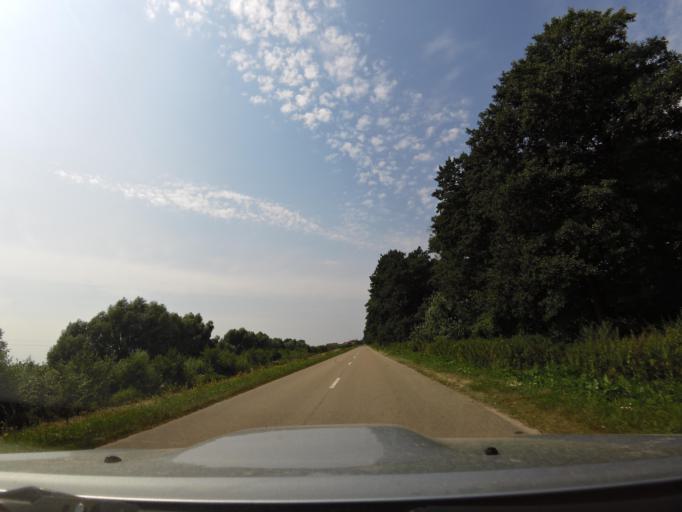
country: LT
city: Rusne
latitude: 55.3453
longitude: 21.3015
